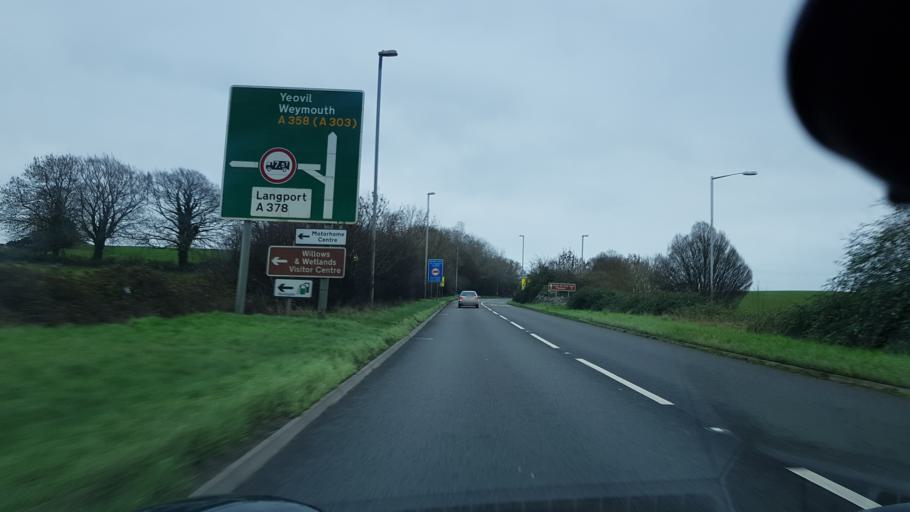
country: GB
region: England
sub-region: Somerset
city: Creech Saint Michael
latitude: 51.0021
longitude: -3.0238
